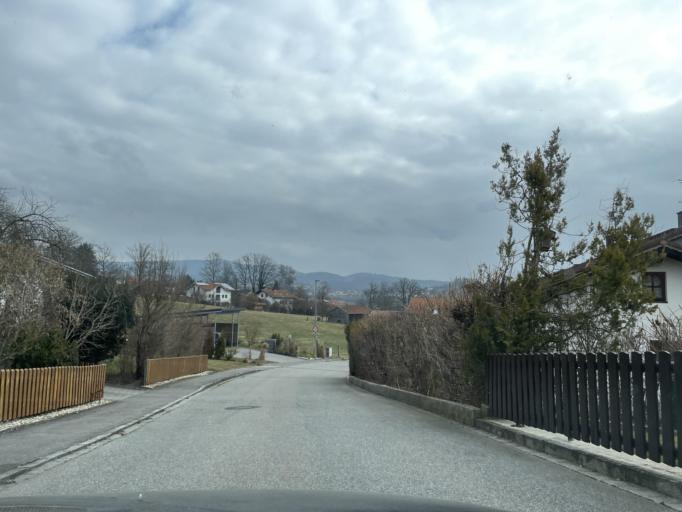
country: DE
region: Bavaria
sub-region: Lower Bavaria
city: Viechtach
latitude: 49.0843
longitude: 12.8793
